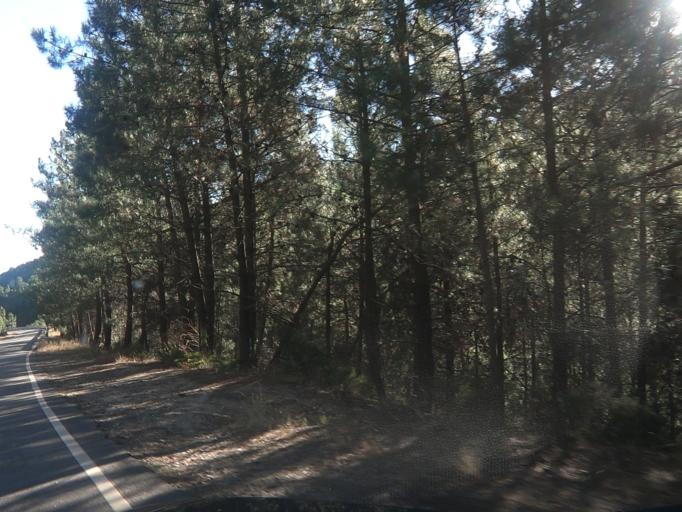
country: PT
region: Vila Real
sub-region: Vila Real
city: Vila Real
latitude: 41.3377
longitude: -7.7784
